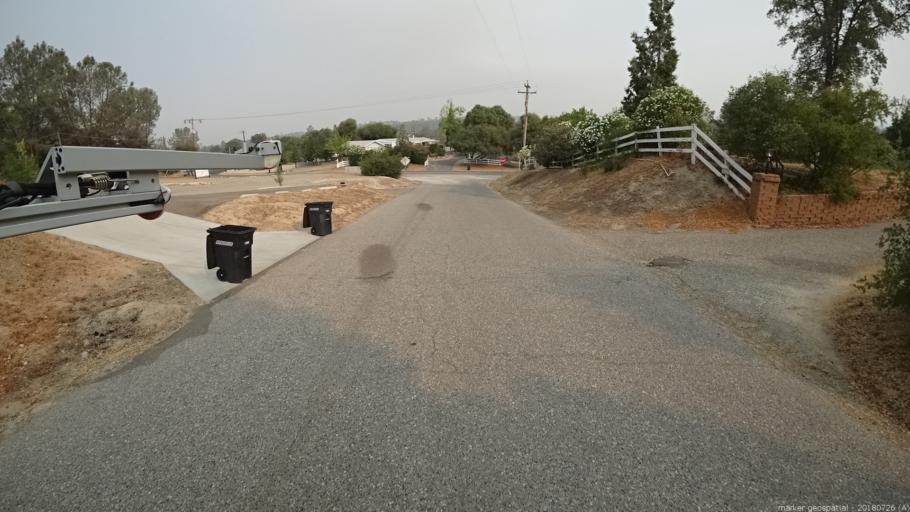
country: US
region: California
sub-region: Madera County
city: Coarsegold
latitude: 37.2185
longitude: -119.7056
